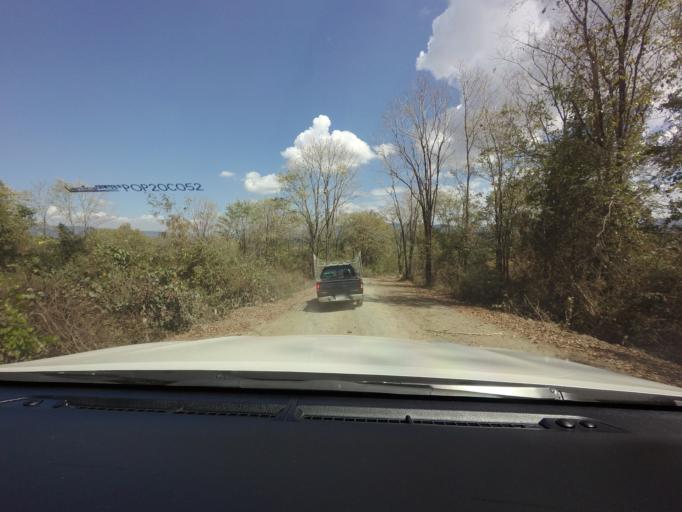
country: TH
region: Nakhon Ratchasima
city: Wang Nam Khiao
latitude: 14.4657
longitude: 101.7804
